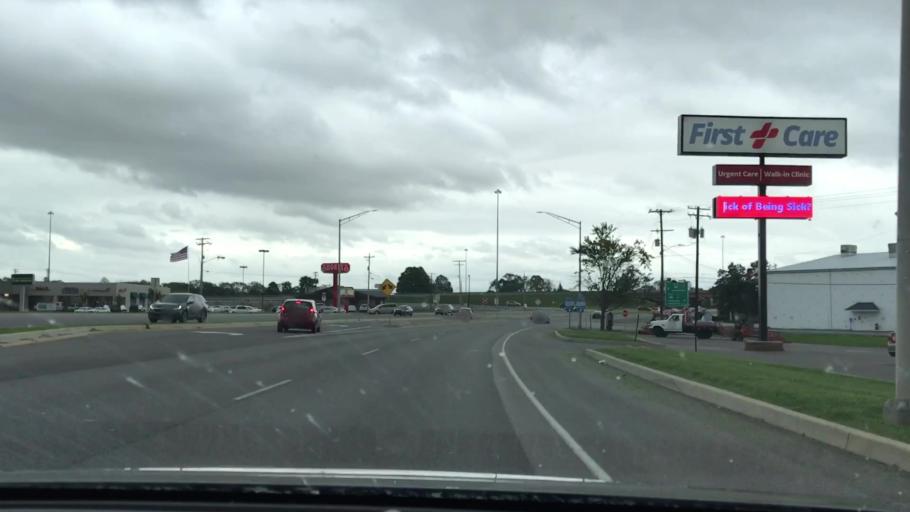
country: US
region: Kentucky
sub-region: Christian County
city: Hopkinsville
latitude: 36.8352
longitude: -87.4751
